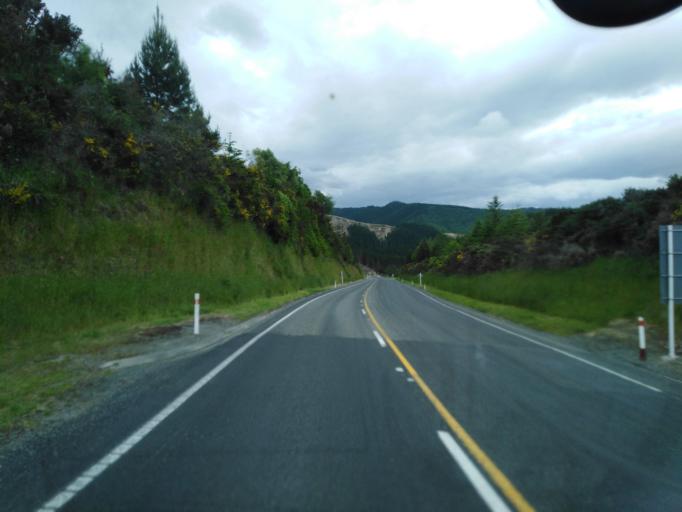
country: NZ
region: Tasman
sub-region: Tasman District
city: Wakefield
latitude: -41.4843
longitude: 172.9051
